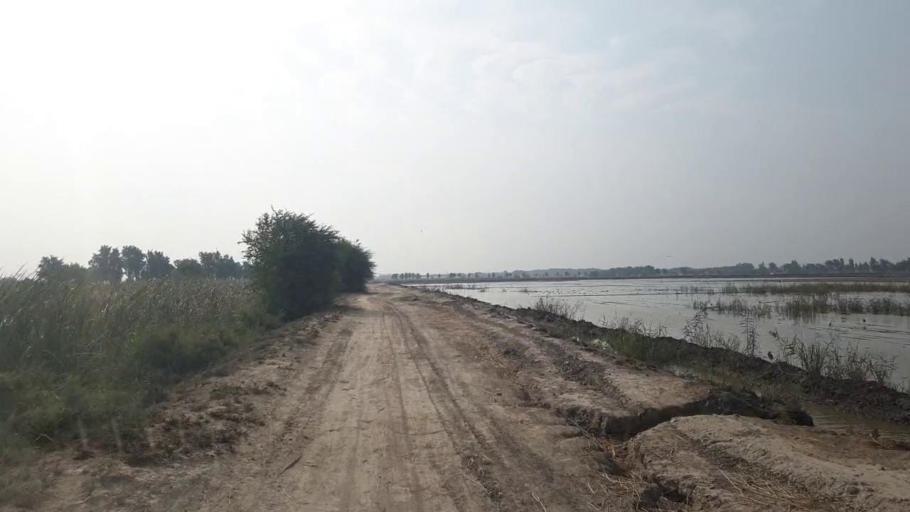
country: PK
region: Sindh
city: Tando Muhammad Khan
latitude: 25.1010
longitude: 68.5066
